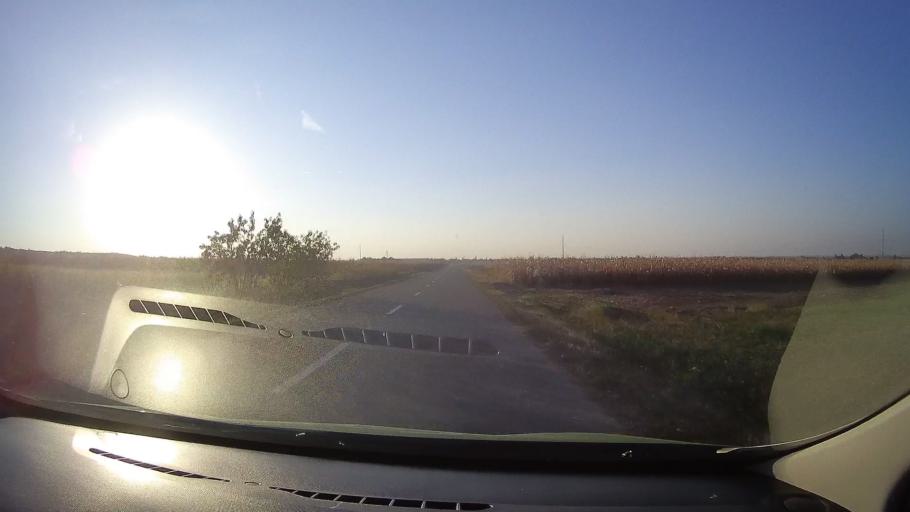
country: RO
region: Bihor
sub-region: Comuna Paleu
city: Paleu
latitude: 47.1615
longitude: 21.9656
